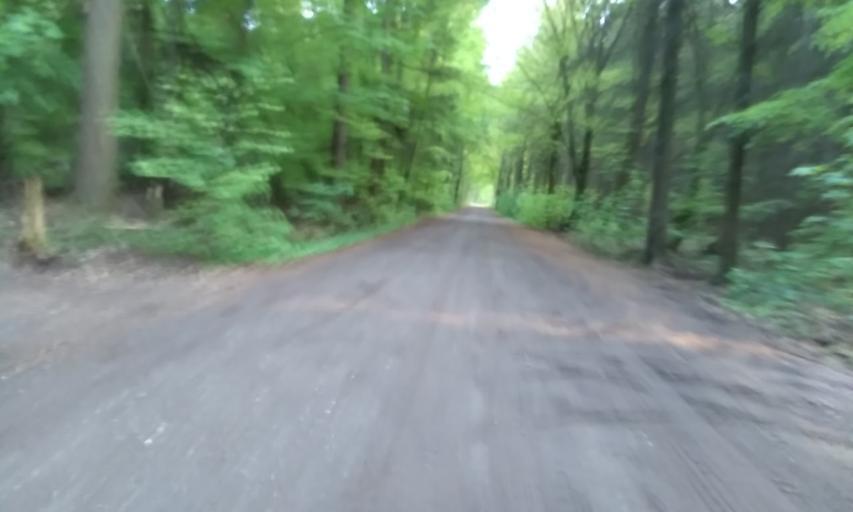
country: DE
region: Lower Saxony
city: Dollern
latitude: 53.5150
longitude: 9.5347
